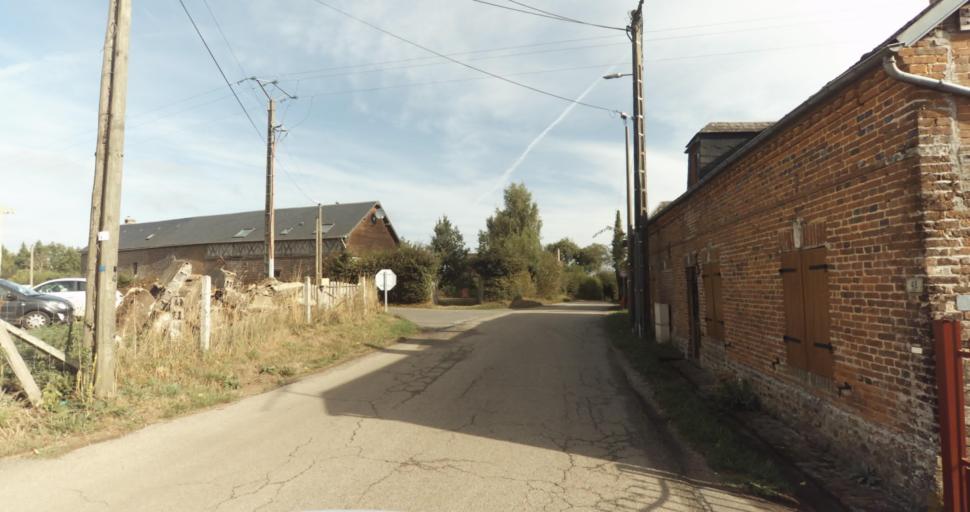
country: FR
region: Lower Normandy
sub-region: Departement de l'Orne
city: Gace
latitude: 48.8912
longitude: 0.3362
